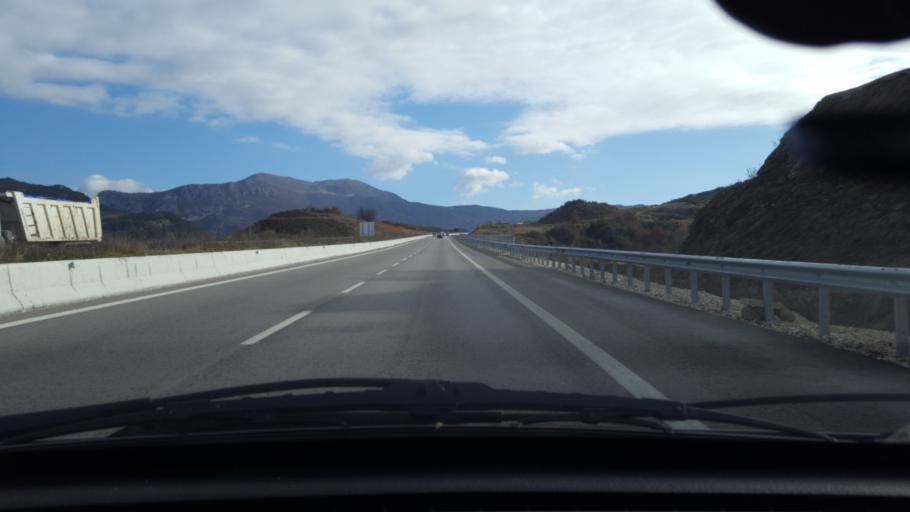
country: AL
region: Tirane
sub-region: Rrethi i Tiranes
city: Krrabe
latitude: 41.2260
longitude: 19.9368
